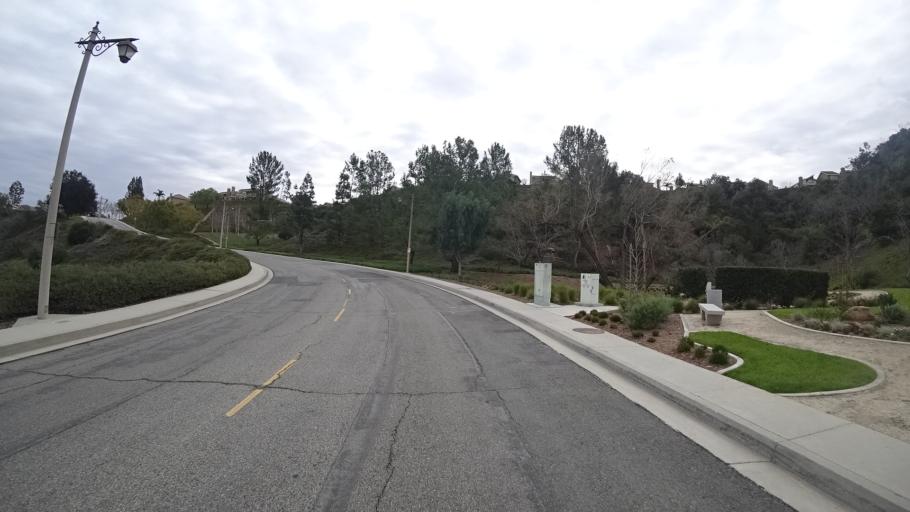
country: US
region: California
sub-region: Orange County
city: Villa Park
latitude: 33.8355
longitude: -117.7778
